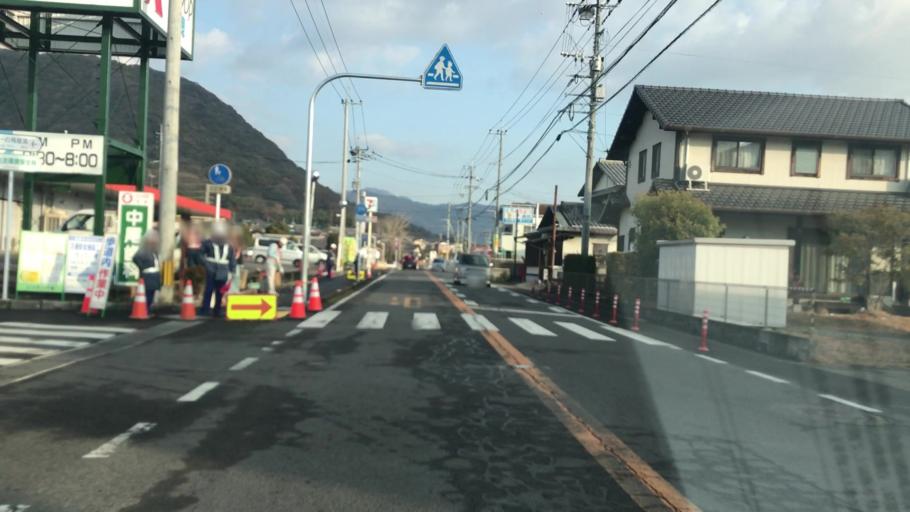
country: JP
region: Saga Prefecture
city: Takeocho-takeo
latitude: 33.2020
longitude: 130.0244
